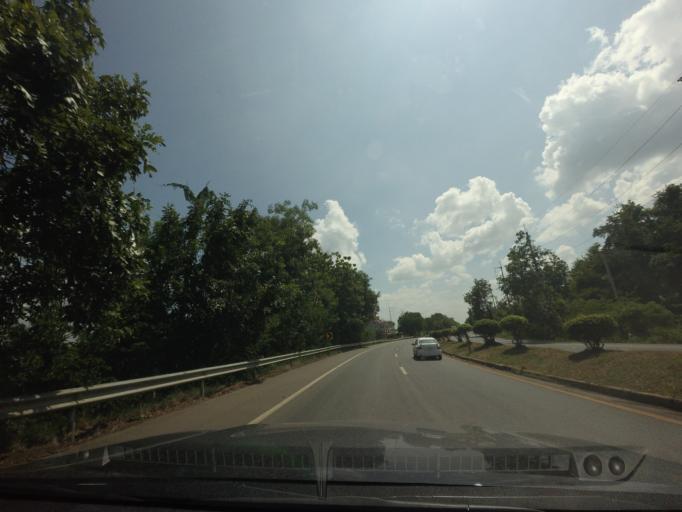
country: TH
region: Phetchabun
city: Nong Phai
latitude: 16.0459
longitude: 101.0809
